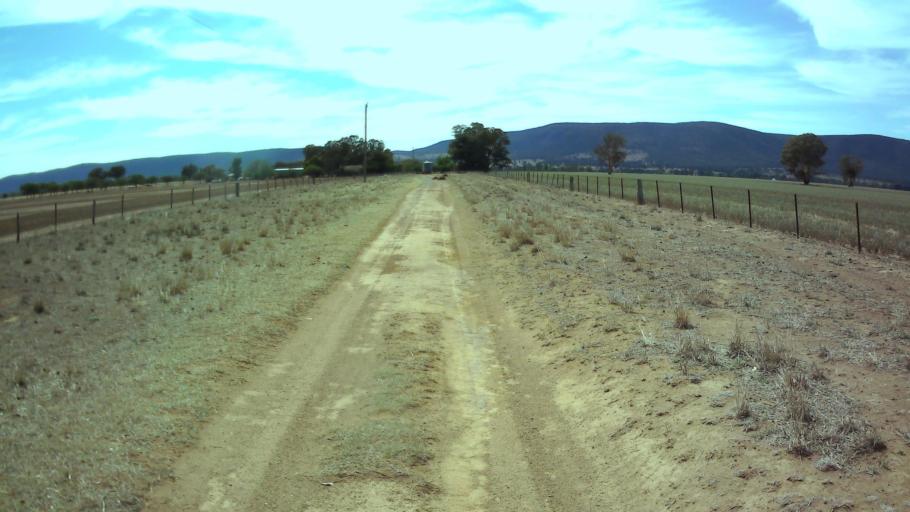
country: AU
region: New South Wales
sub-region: Weddin
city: Grenfell
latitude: -33.7222
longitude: 148.2705
